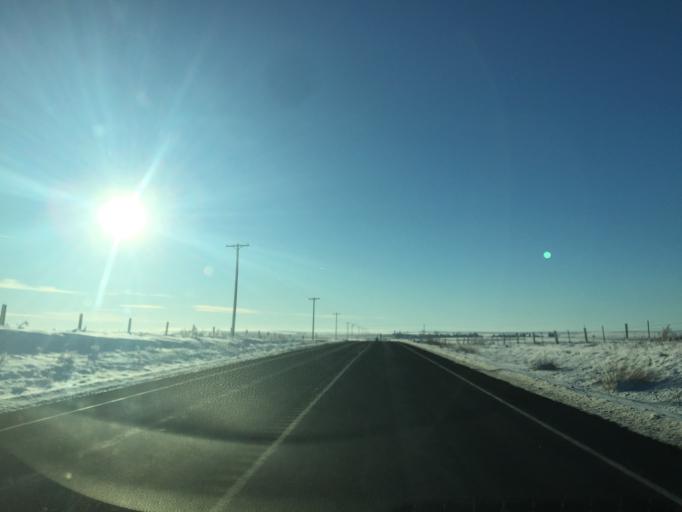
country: US
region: Washington
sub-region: Okanogan County
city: Coulee Dam
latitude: 47.7227
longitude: -118.8910
